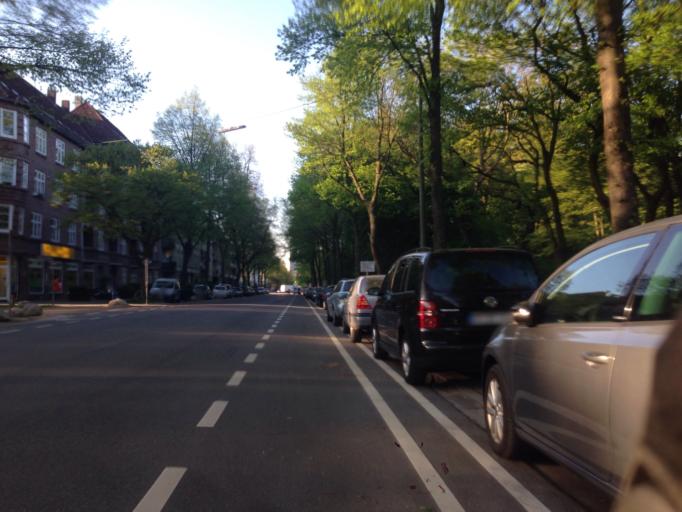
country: DE
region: Hamburg
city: Borgfelde
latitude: 53.5589
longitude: 10.0543
